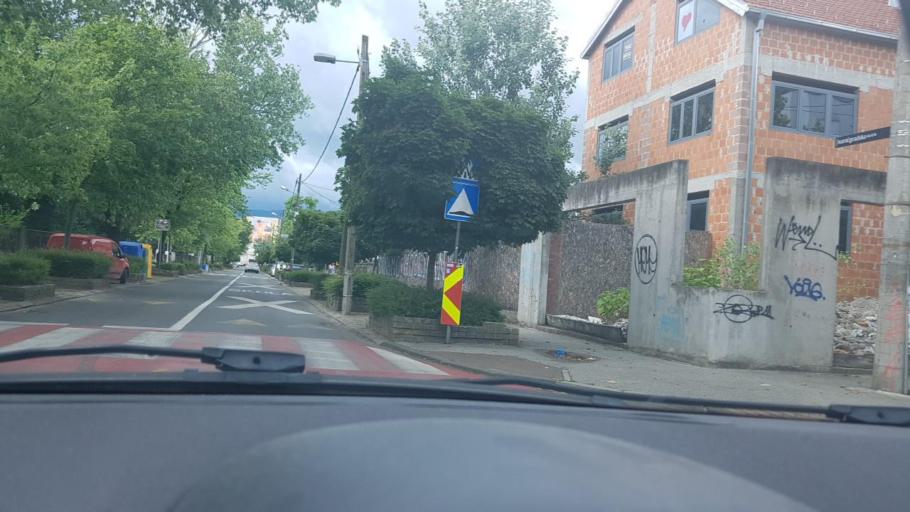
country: HR
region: Grad Zagreb
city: Zagreb
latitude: 45.8071
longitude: 16.0185
